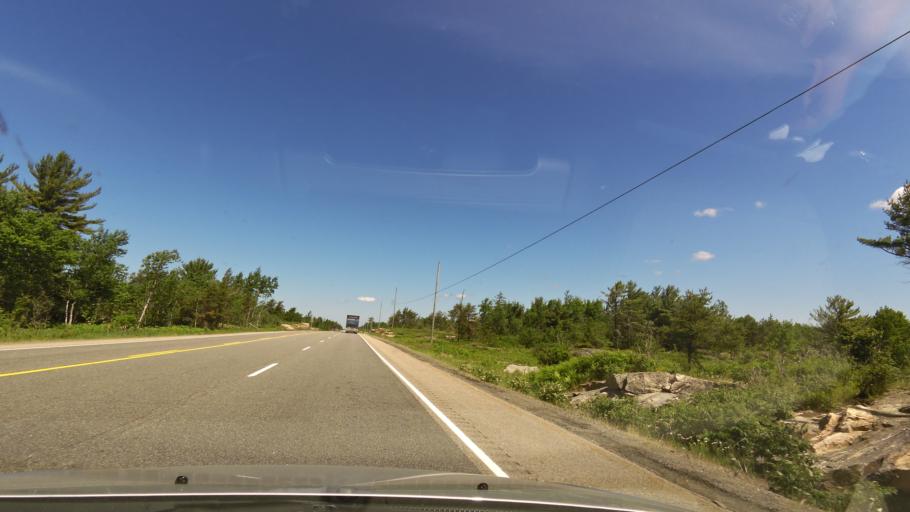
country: CA
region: Ontario
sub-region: Parry Sound District
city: Parry Sound
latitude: 45.7120
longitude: -80.4626
